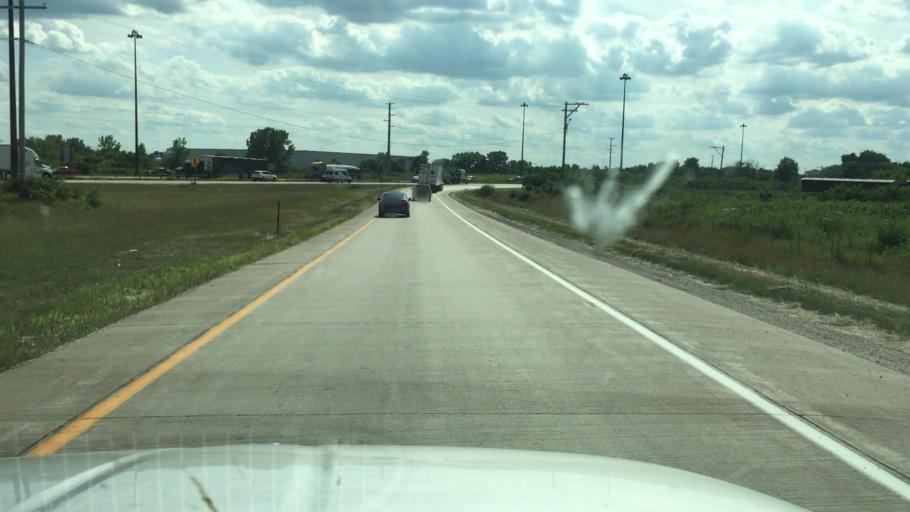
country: US
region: Illinois
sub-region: LaSalle County
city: Deer Park
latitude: 41.3685
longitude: -89.0127
